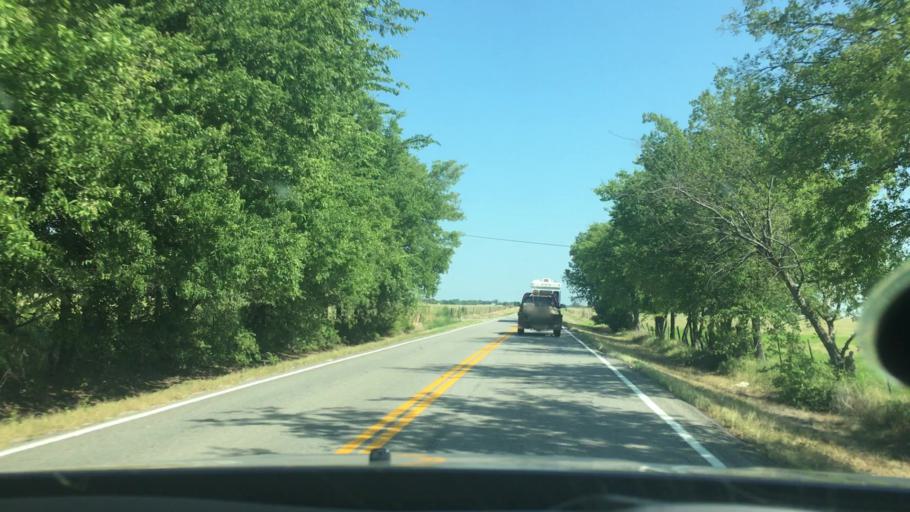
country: US
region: Oklahoma
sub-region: Johnston County
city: Tishomingo
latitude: 34.1642
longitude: -96.5085
